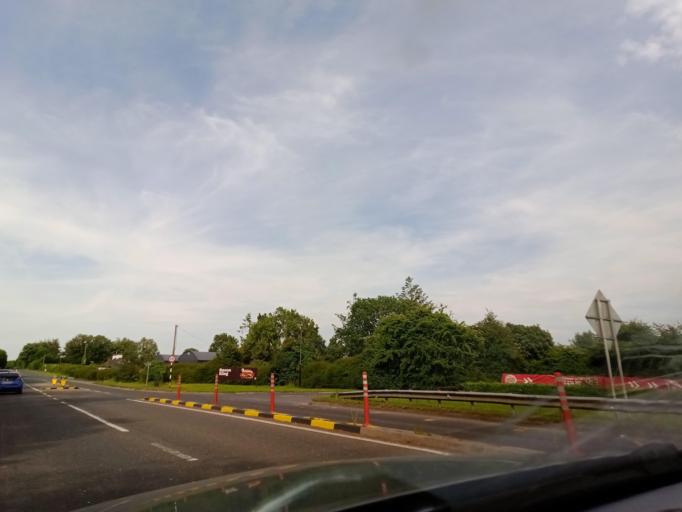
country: IE
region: Leinster
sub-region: Laois
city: Portlaoise
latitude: 53.0156
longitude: -7.3020
